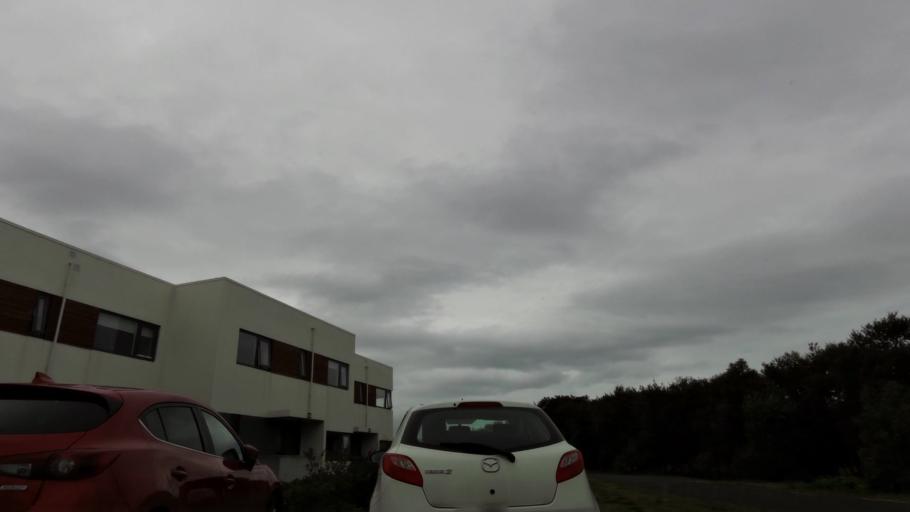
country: IS
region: Capital Region
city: Reykjavik
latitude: 64.1169
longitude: -21.8902
